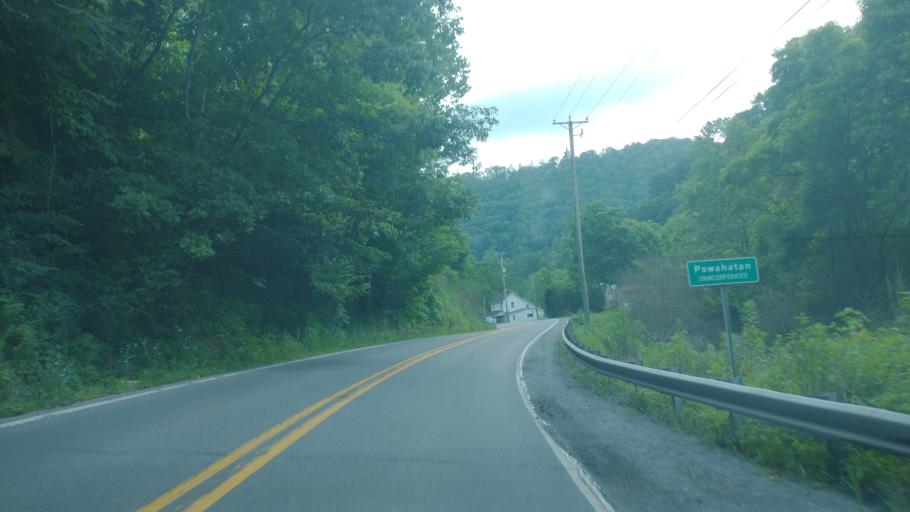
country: US
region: West Virginia
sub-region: McDowell County
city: Welch
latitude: 37.3984
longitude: -81.4221
